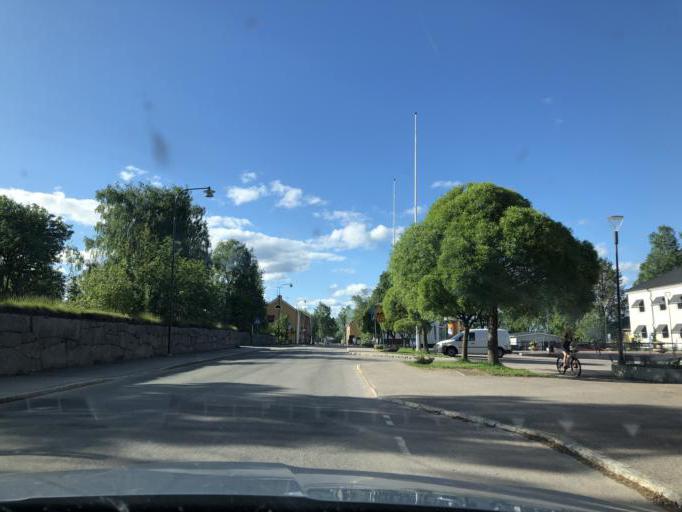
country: SE
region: Norrbotten
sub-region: Overkalix Kommun
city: OEverkalix
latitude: 66.3268
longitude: 22.8448
